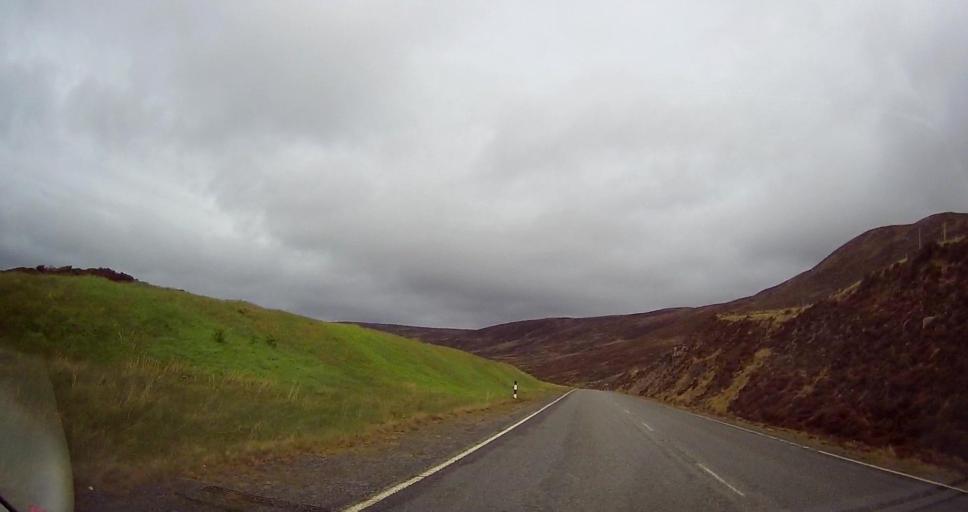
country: GB
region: Scotland
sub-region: Shetland Islands
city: Lerwick
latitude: 60.3592
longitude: -1.2853
